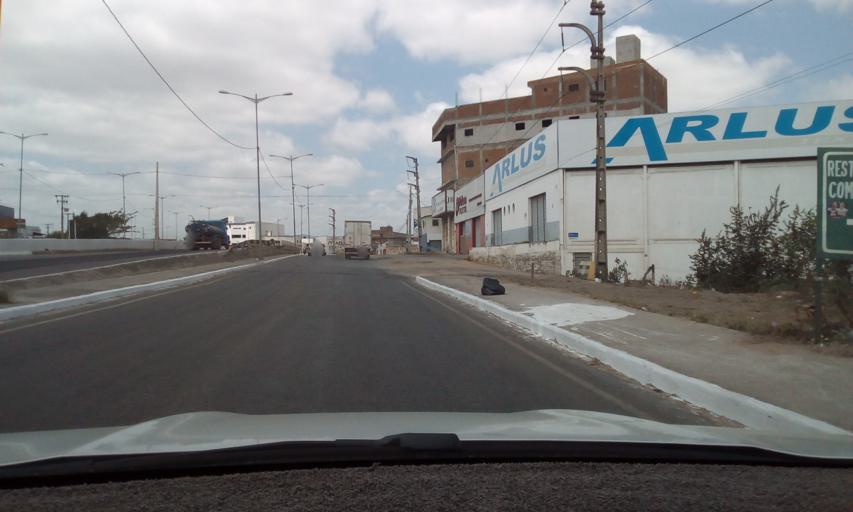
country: BR
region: Pernambuco
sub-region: Caruaru
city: Caruaru
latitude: -8.2713
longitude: -35.9816
